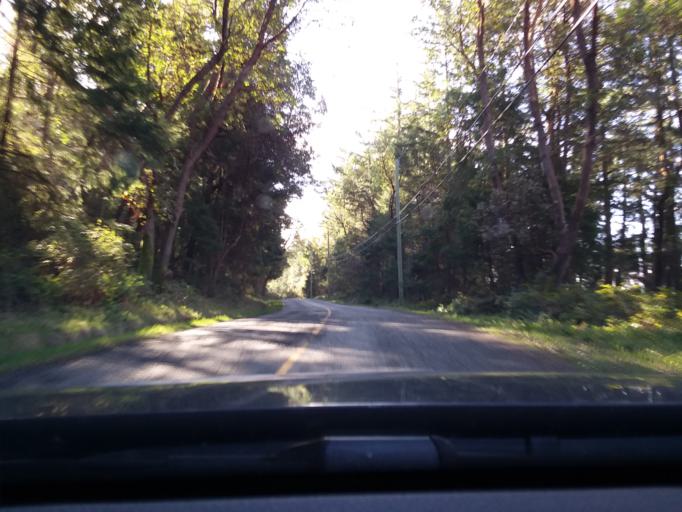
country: CA
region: British Columbia
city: North Cowichan
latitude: 48.9639
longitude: -123.5499
